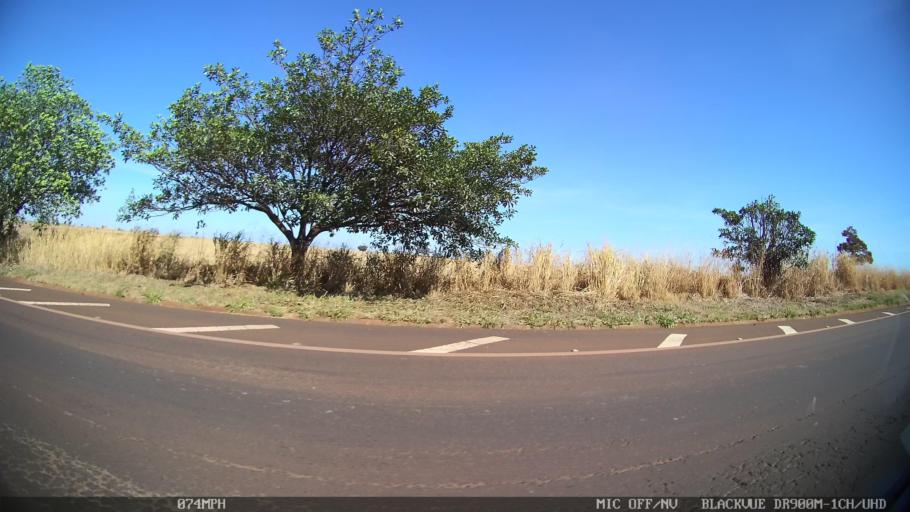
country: BR
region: Sao Paulo
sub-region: Ipua
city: Ipua
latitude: -20.4795
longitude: -48.0828
